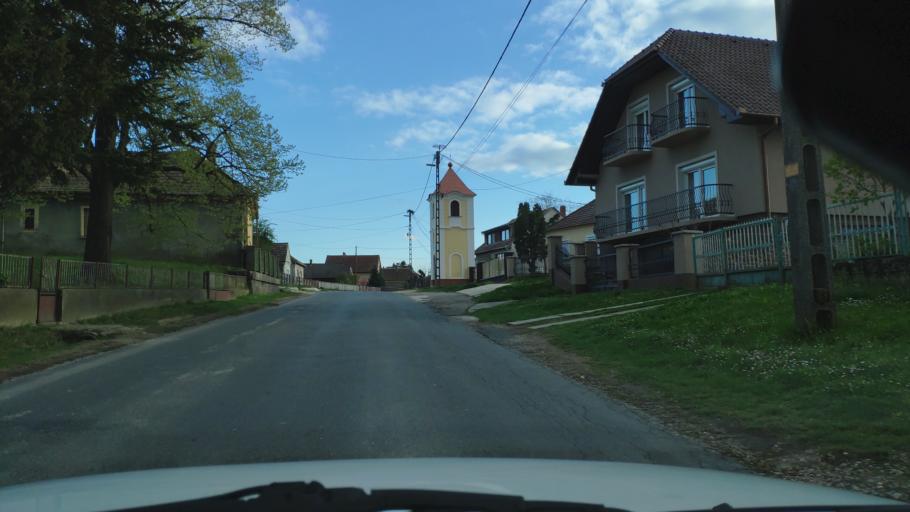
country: HU
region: Zala
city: Zalakomar
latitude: 46.4863
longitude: 17.1299
